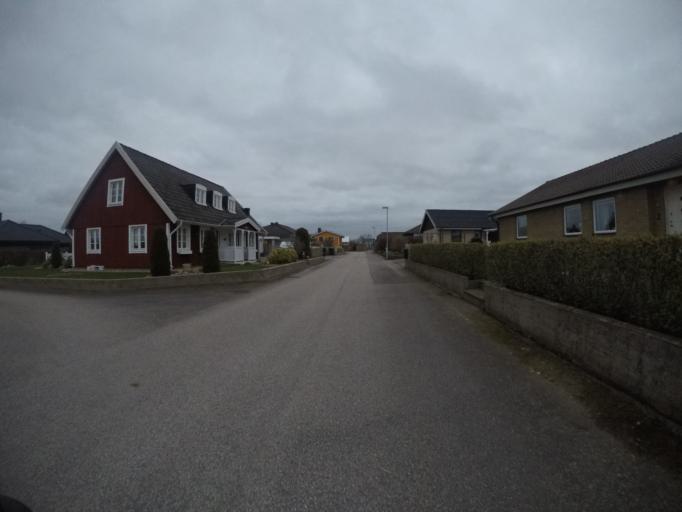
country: SE
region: Halland
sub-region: Laholms Kommun
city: Laholm
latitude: 56.5071
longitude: 13.0224
